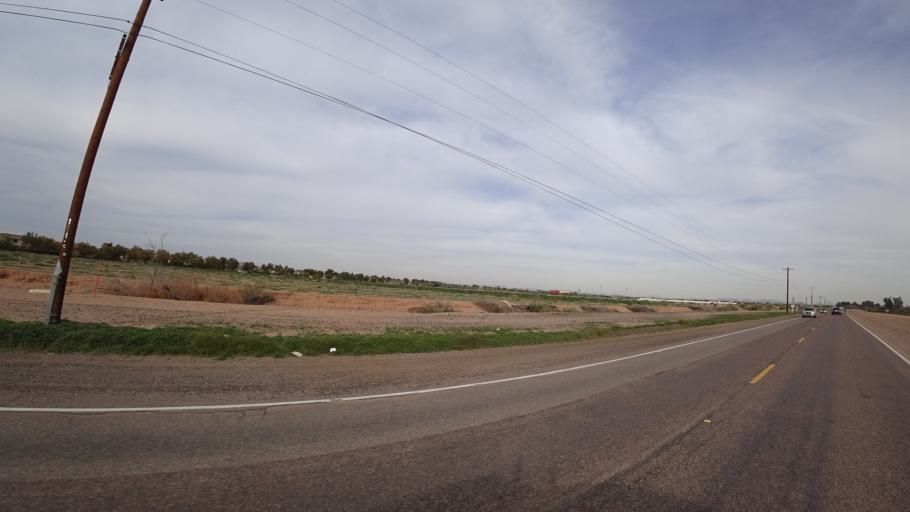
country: US
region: Arizona
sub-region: Maricopa County
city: Citrus Park
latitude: 33.5805
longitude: -112.3884
